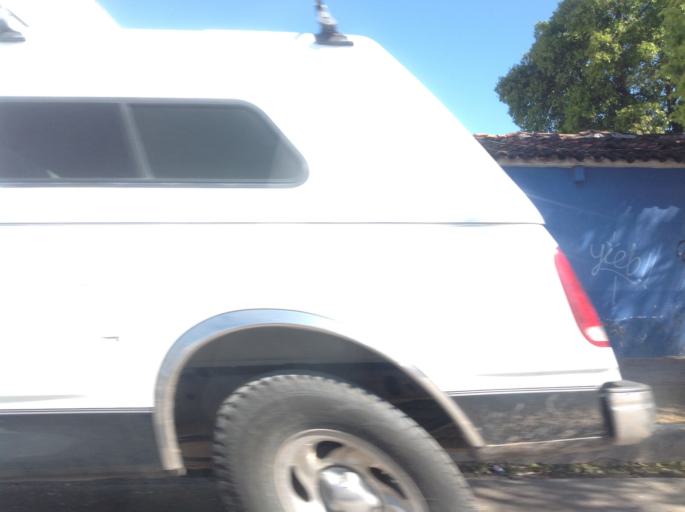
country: MX
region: Oaxaca
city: Ciudad de Huajuapam de Leon
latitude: 17.8115
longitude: -97.7716
